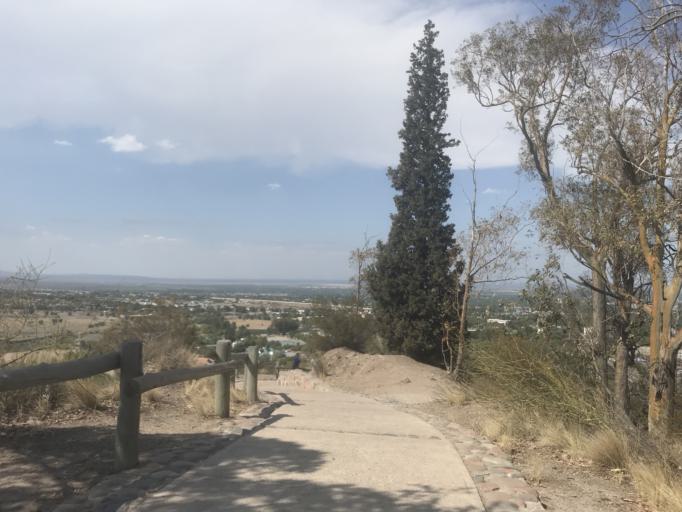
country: AR
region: Mendoza
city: Mendoza
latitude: -32.8860
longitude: -68.8900
